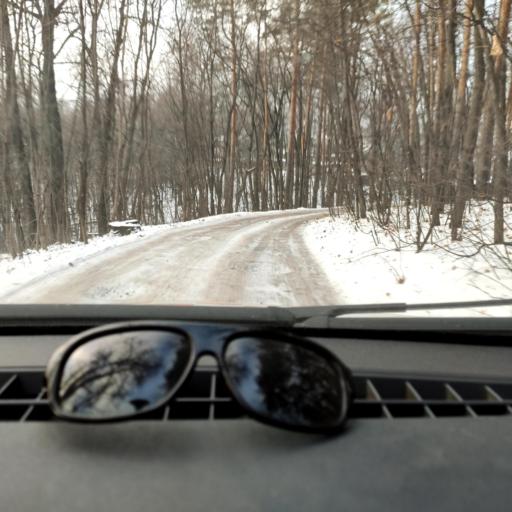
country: RU
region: Bashkortostan
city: Ufa
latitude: 54.7467
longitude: 56.0065
